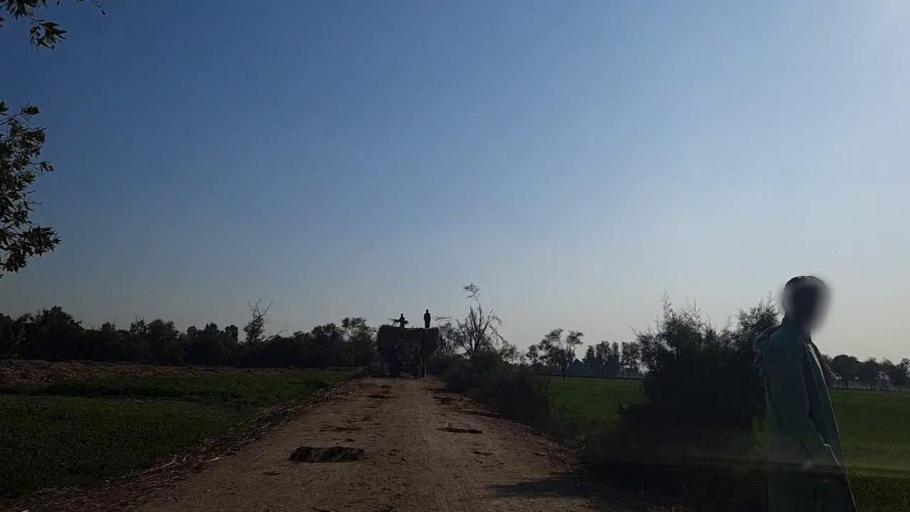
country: PK
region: Sindh
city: Sakrand
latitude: 26.3110
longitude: 68.1819
